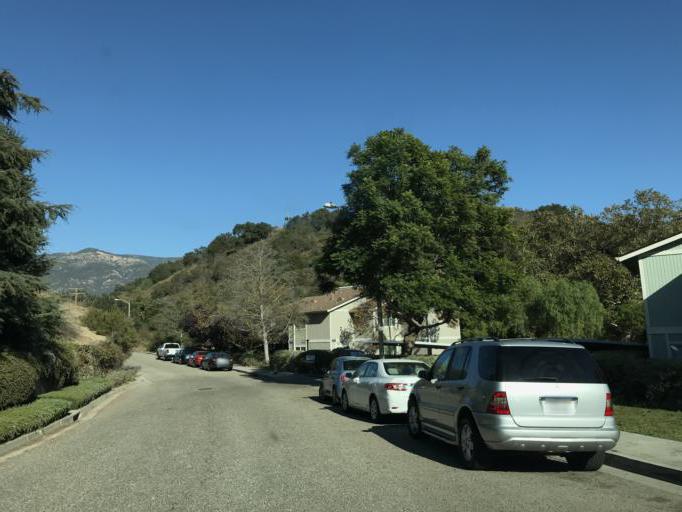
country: US
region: California
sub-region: Santa Barbara County
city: Goleta
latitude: 34.4471
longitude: -119.7788
